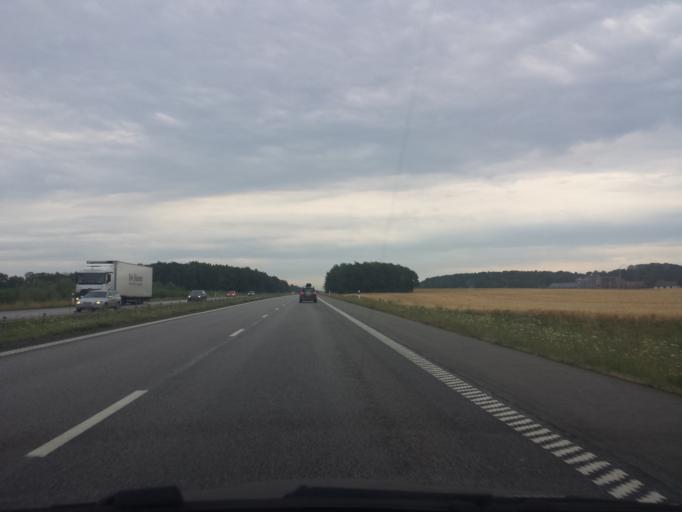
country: SE
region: Skane
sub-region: Malmo
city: Oxie
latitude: 55.5481
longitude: 13.1350
